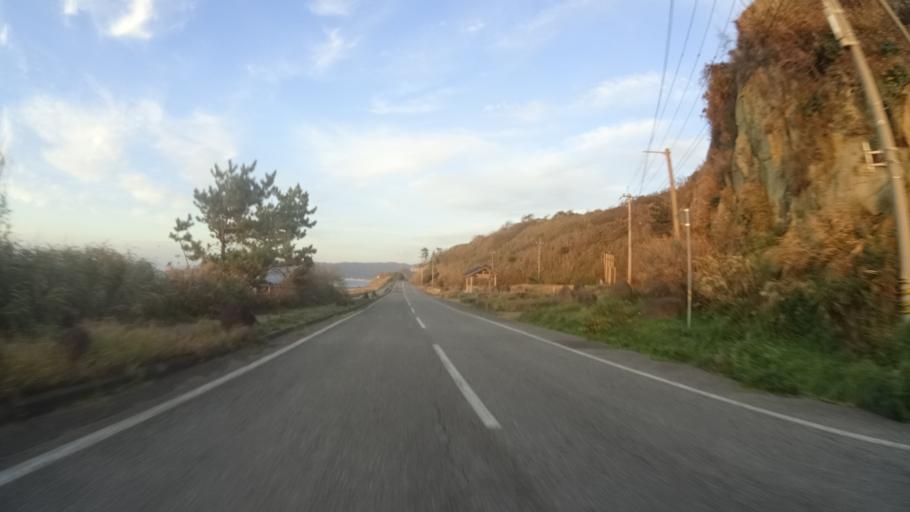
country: JP
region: Ishikawa
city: Nanao
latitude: 37.2516
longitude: 136.7169
